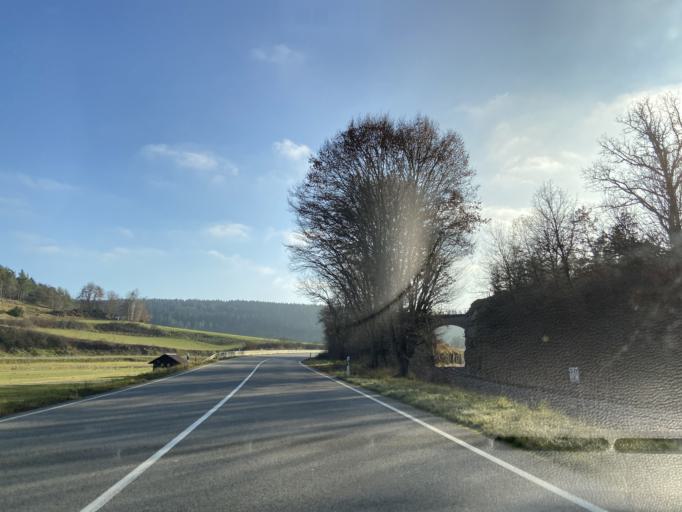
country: DE
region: Baden-Wuerttemberg
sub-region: Tuebingen Region
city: Veringenstadt
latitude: 48.1767
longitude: 9.2079
